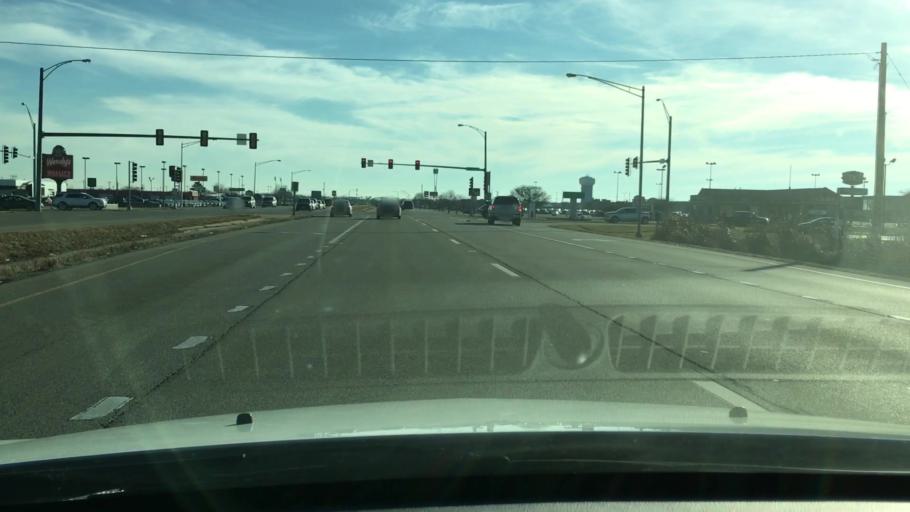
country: US
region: Illinois
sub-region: LaSalle County
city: Peru
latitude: 41.3595
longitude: -89.1256
